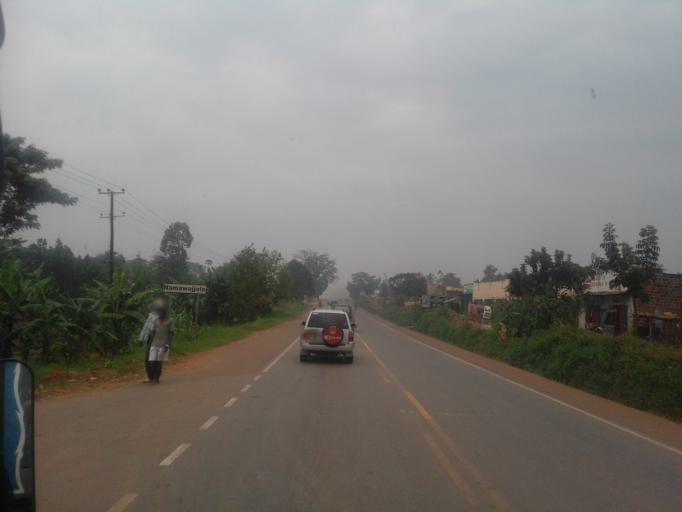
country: UG
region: Central Region
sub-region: Mukono District
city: Mukono
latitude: 0.3815
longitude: 32.8347
